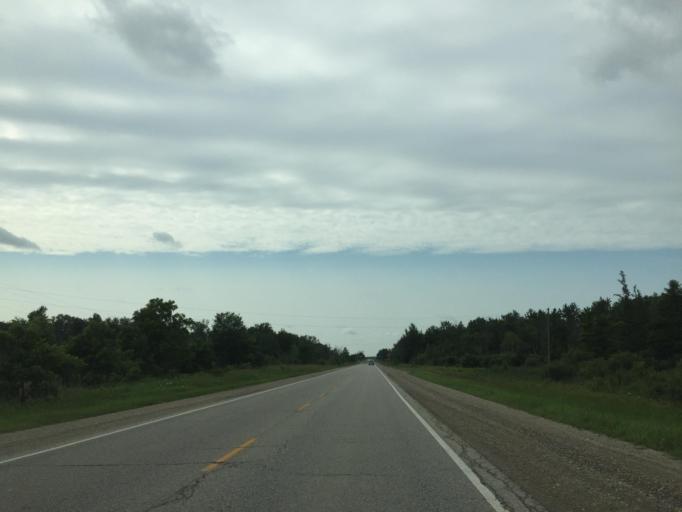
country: CA
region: Ontario
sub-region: Wellington County
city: Guelph
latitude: 43.5527
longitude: -80.3339
